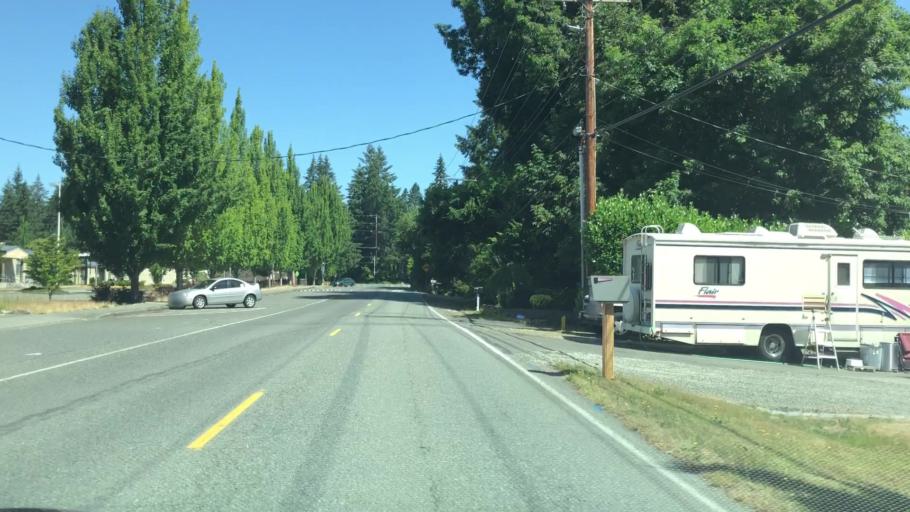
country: US
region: Washington
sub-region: Snohomish County
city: Maltby
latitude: 47.7667
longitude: -122.1156
